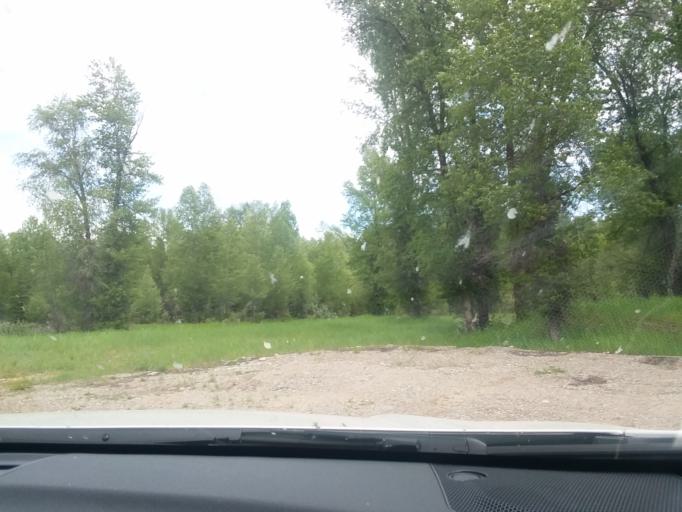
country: US
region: Wyoming
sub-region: Teton County
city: Moose Wilson Road
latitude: 43.5046
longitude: -110.8427
